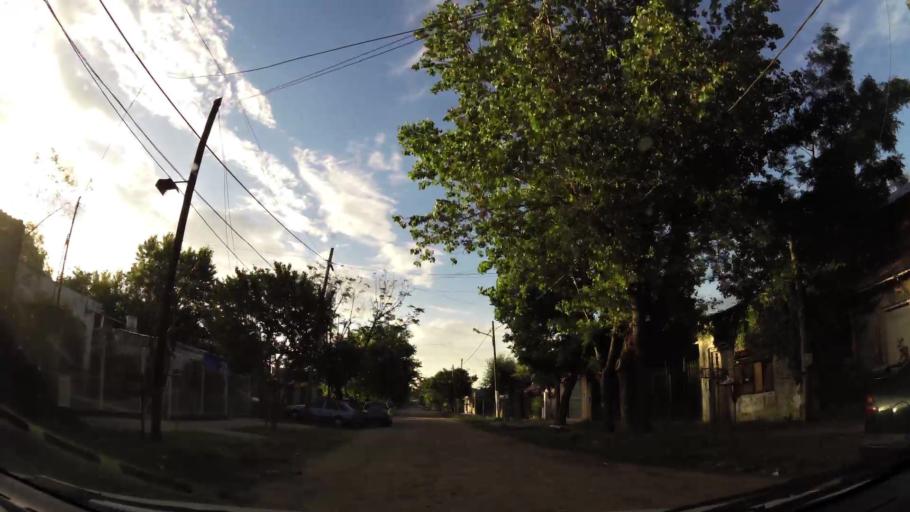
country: AR
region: Buenos Aires
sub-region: Partido de Merlo
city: Merlo
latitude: -34.6796
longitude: -58.7516
